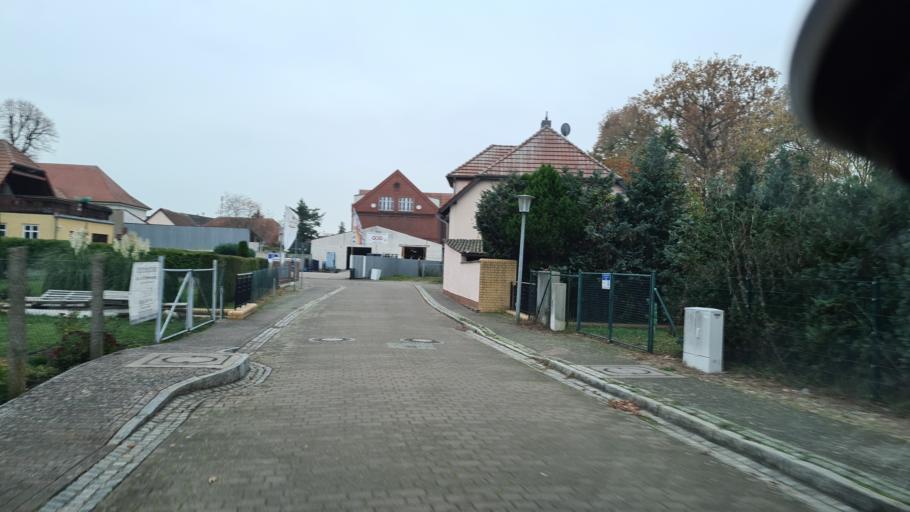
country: DE
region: Brandenburg
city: Lindow
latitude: 52.9703
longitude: 12.9851
